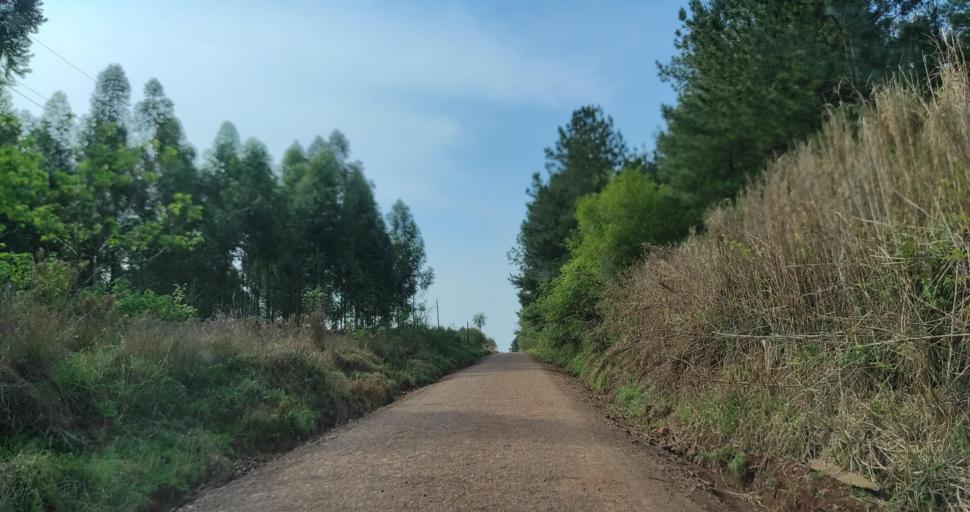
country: AR
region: Misiones
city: Garuhape
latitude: -26.8691
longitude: -55.0053
